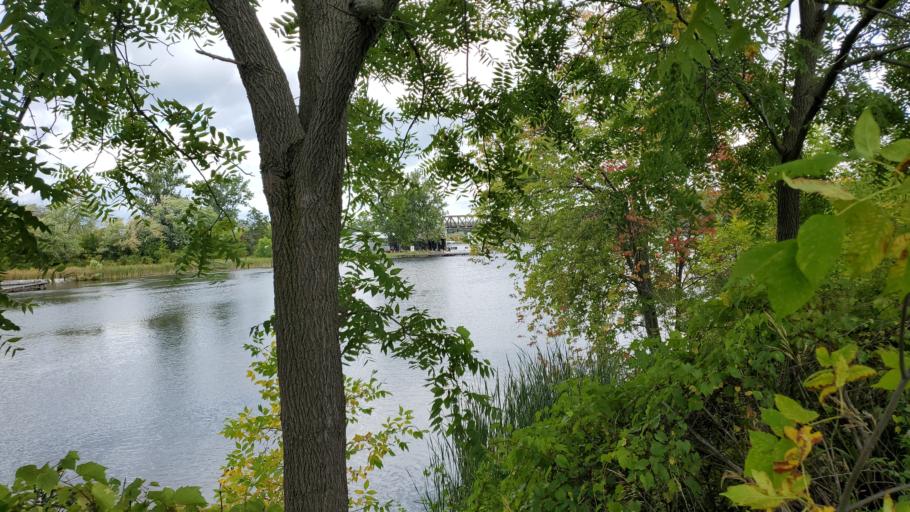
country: CA
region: Ontario
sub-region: Lanark County
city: Smiths Falls
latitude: 44.9175
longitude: -75.8342
